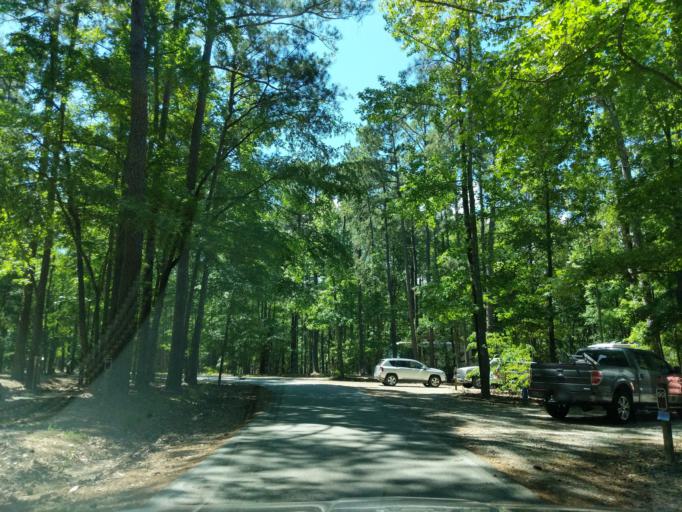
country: US
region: Georgia
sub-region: Columbia County
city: Appling
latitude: 33.6656
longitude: -82.3852
